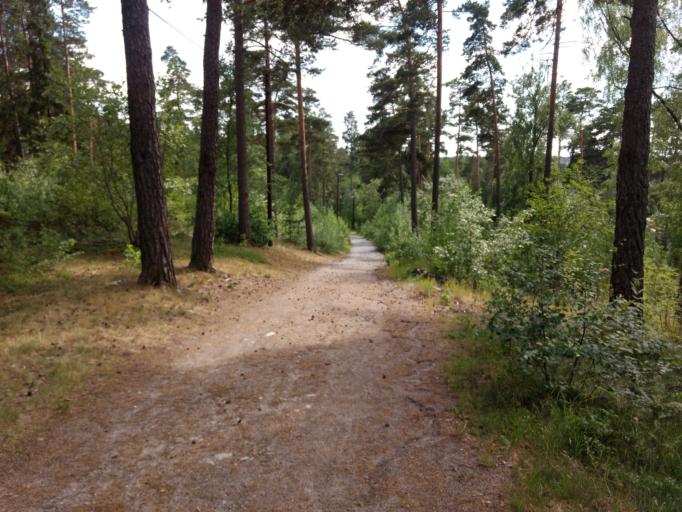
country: SE
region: Stockholm
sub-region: Upplands Vasby Kommun
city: Upplands Vaesby
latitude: 59.5231
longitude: 17.9222
